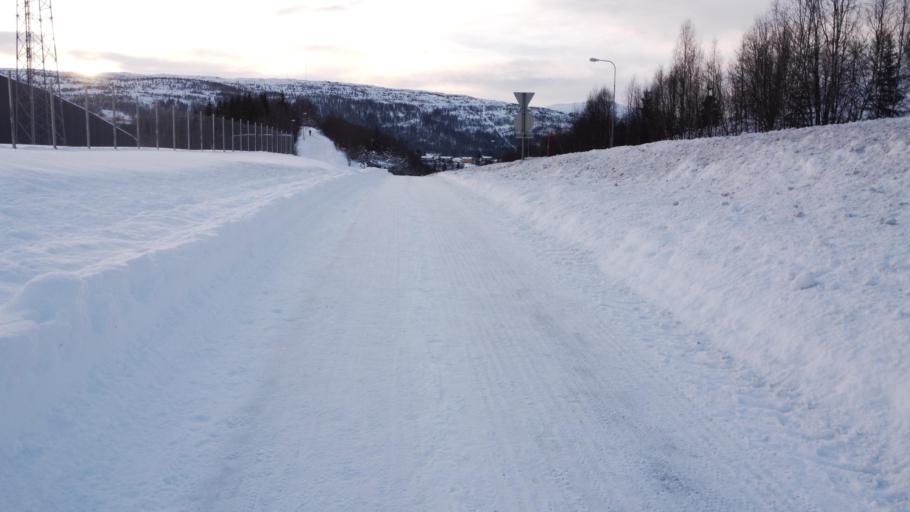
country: NO
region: Nordland
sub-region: Rana
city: Mo i Rana
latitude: 66.3233
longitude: 14.1584
